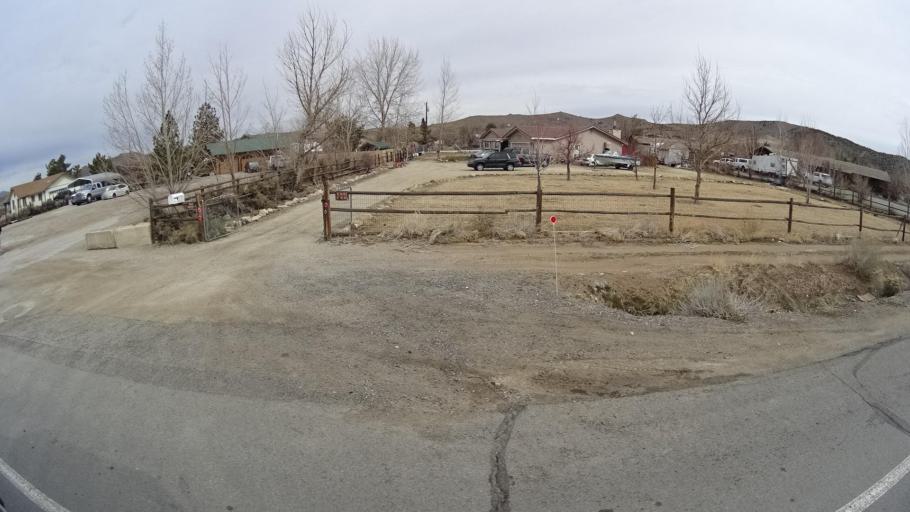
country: US
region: Nevada
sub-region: Washoe County
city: Golden Valley
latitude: 39.6078
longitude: -119.8209
